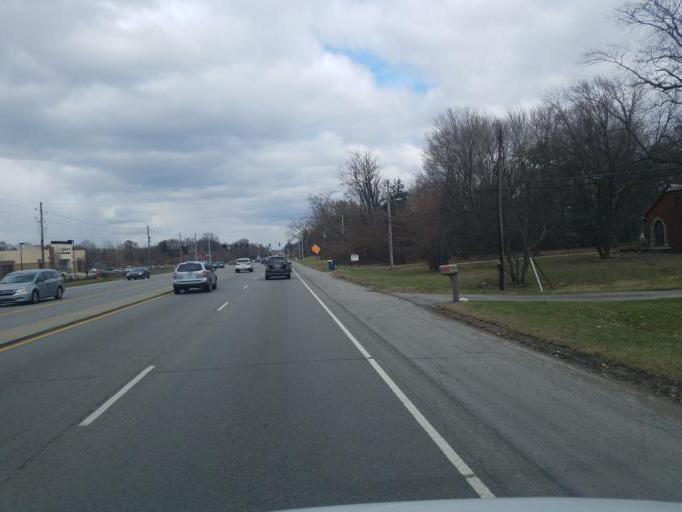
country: US
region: Indiana
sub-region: Marion County
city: Clermont
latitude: 39.7637
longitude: -86.3246
